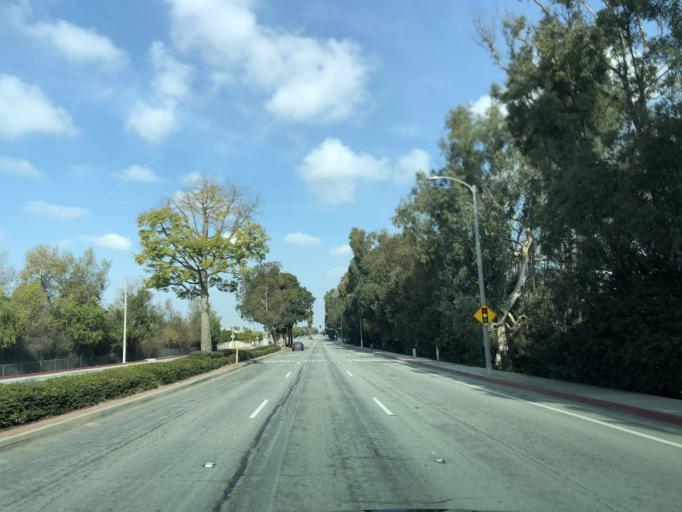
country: US
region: California
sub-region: Orange County
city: Huntington Beach
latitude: 33.7030
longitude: -118.0064
